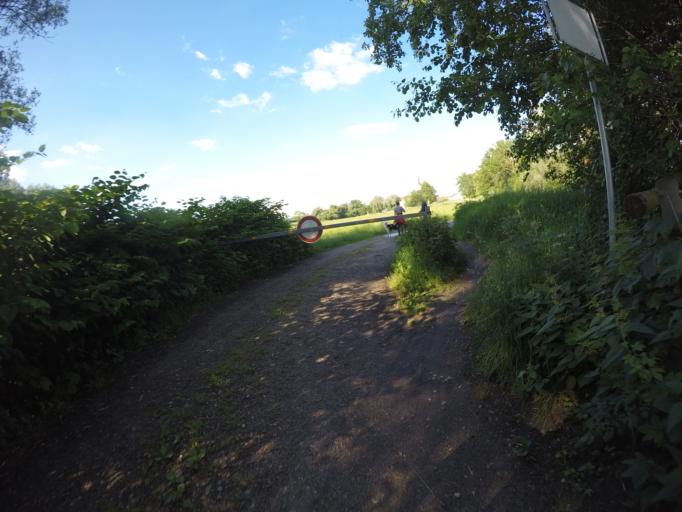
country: DE
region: Bavaria
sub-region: Lower Bavaria
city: Frontenhausen
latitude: 48.5533
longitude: 12.5480
